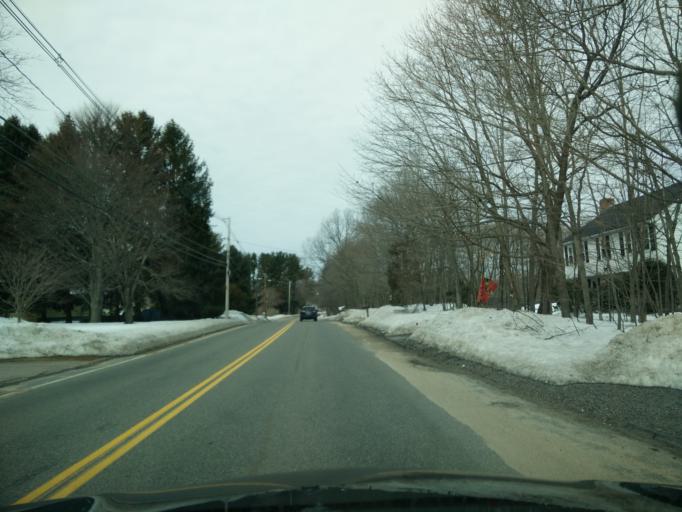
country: US
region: Massachusetts
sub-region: Norfolk County
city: Walpole
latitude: 42.1735
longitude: -71.2417
